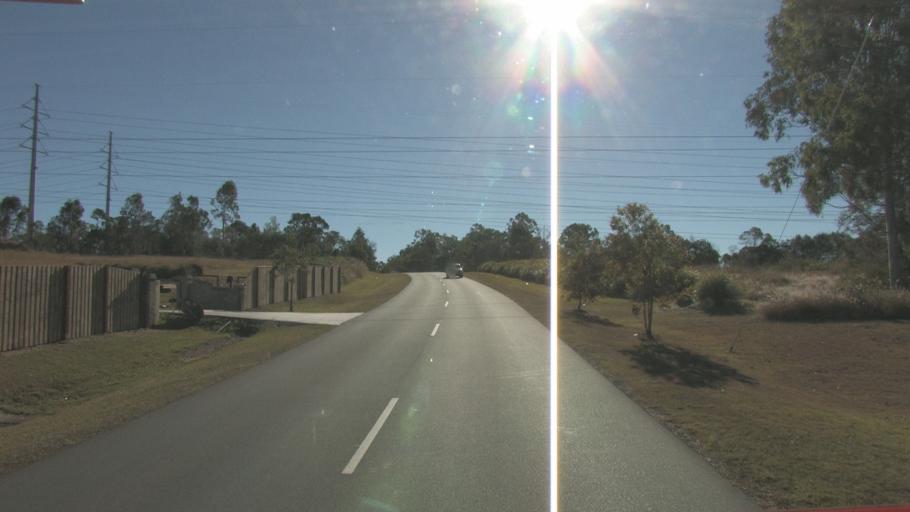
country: AU
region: Queensland
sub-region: Logan
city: North Maclean
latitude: -27.7393
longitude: 152.9695
